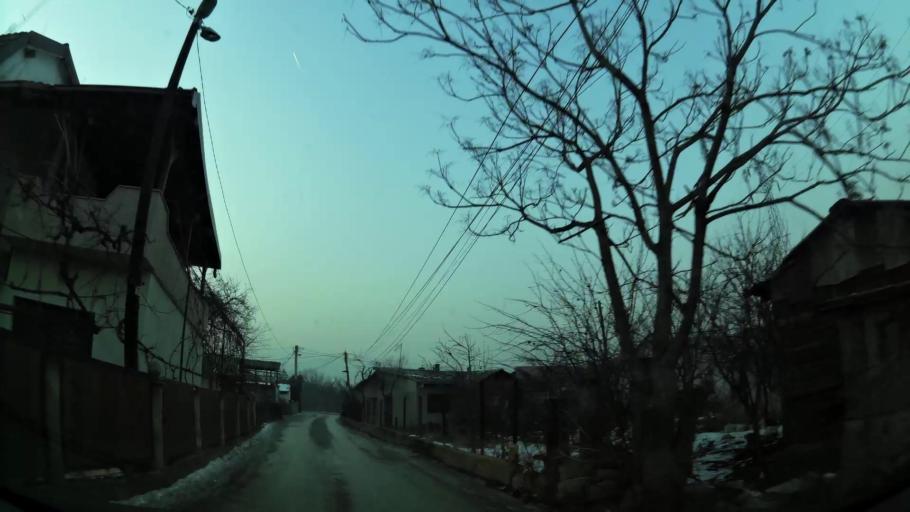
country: MK
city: Creshevo
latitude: 42.0027
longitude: 21.5086
